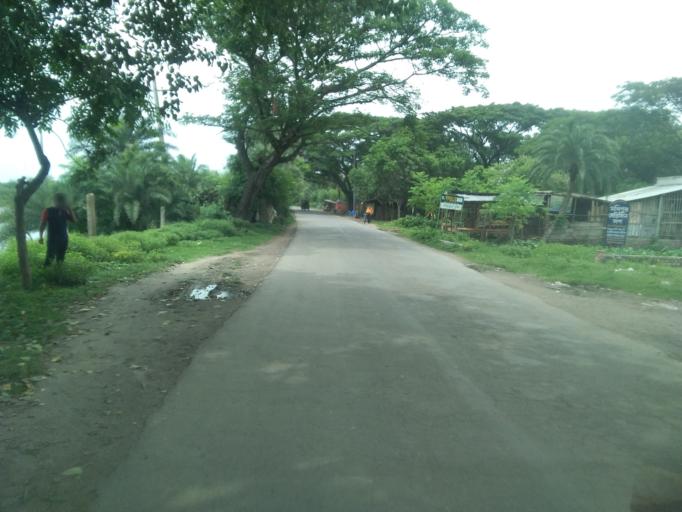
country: IN
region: West Bengal
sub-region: North 24 Parganas
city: Taki
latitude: 22.5808
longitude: 88.9983
